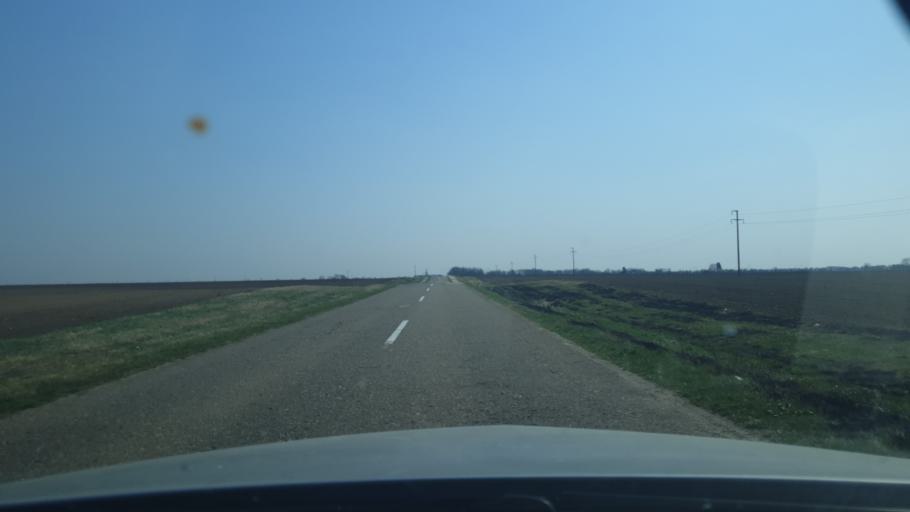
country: RS
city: Sasinci
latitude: 45.0270
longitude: 19.7579
